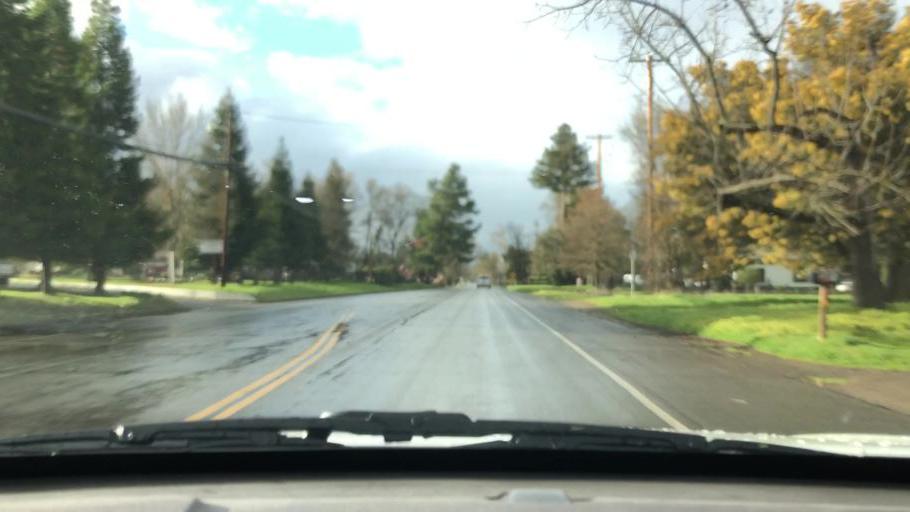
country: US
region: California
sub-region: Mendocino County
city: Talmage
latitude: 39.1124
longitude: -123.1980
